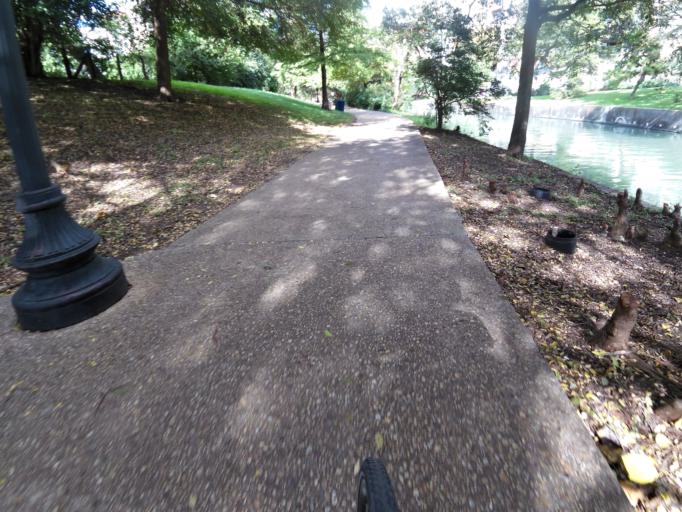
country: US
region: Texas
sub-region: Bexar County
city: San Antonio
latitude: 29.4182
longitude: -98.4929
